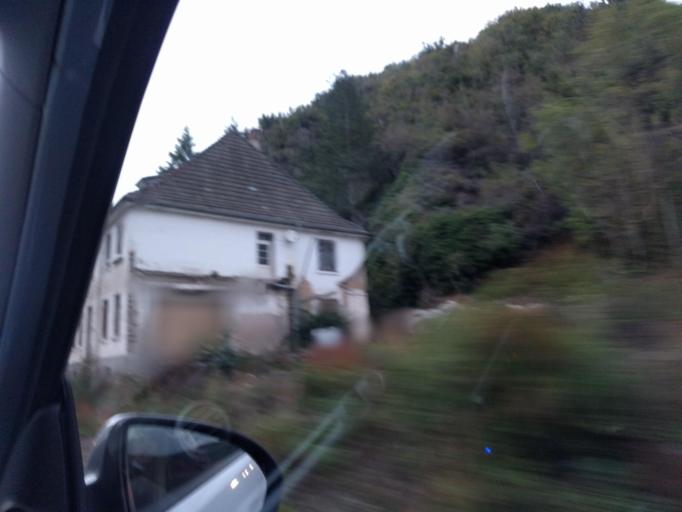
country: DE
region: Rheinland-Pfalz
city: Rech
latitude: 50.5181
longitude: 7.0271
